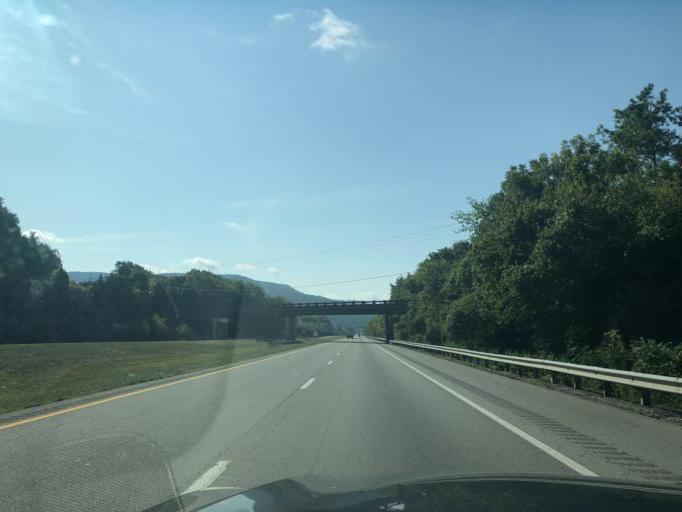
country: US
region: Tennessee
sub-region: Marion County
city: Kimball
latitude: 35.1144
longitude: -85.7493
